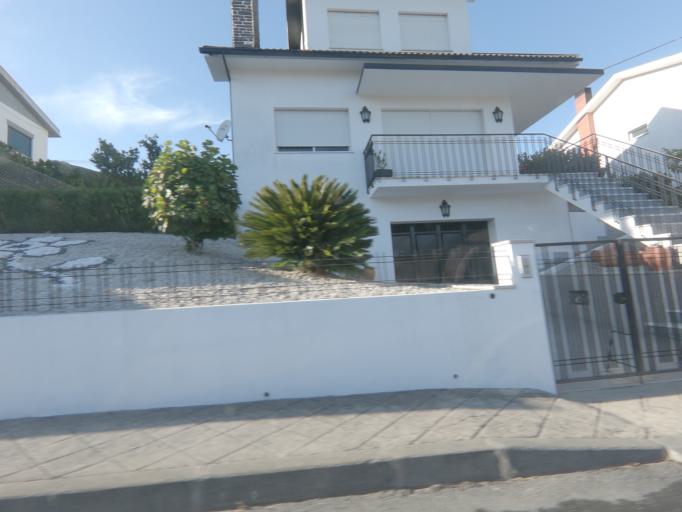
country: PT
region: Vila Real
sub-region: Peso da Regua
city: Godim
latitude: 41.1711
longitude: -7.8046
